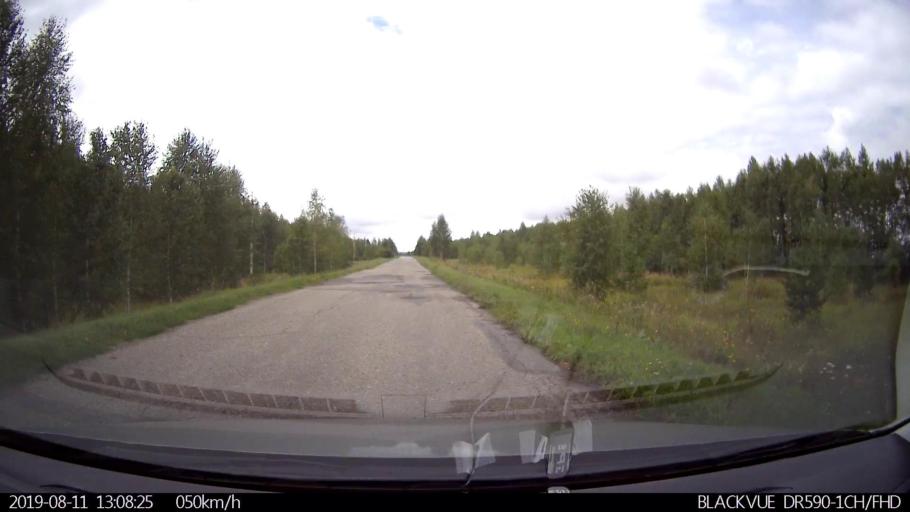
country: RU
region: Ulyanovsk
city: Ignatovka
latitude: 53.8588
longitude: 47.6342
